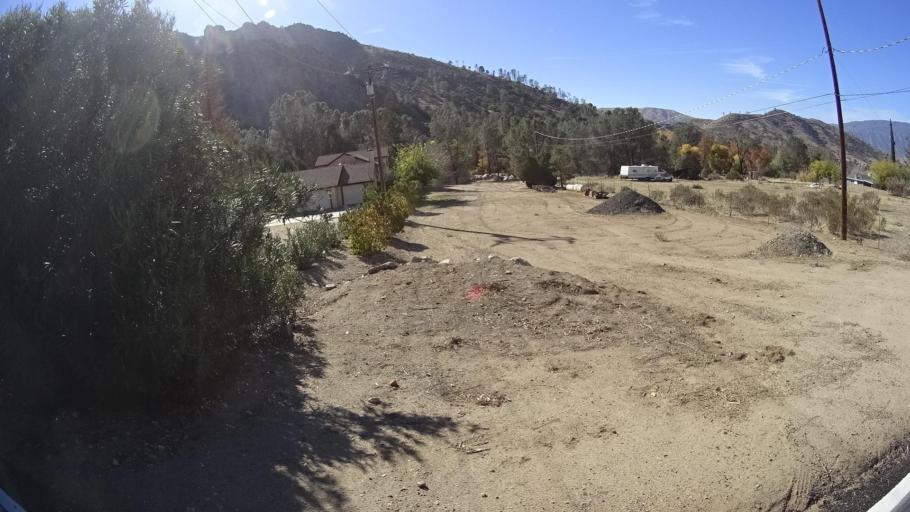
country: US
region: California
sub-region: Kern County
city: Lake Isabella
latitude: 35.5969
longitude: -118.4524
